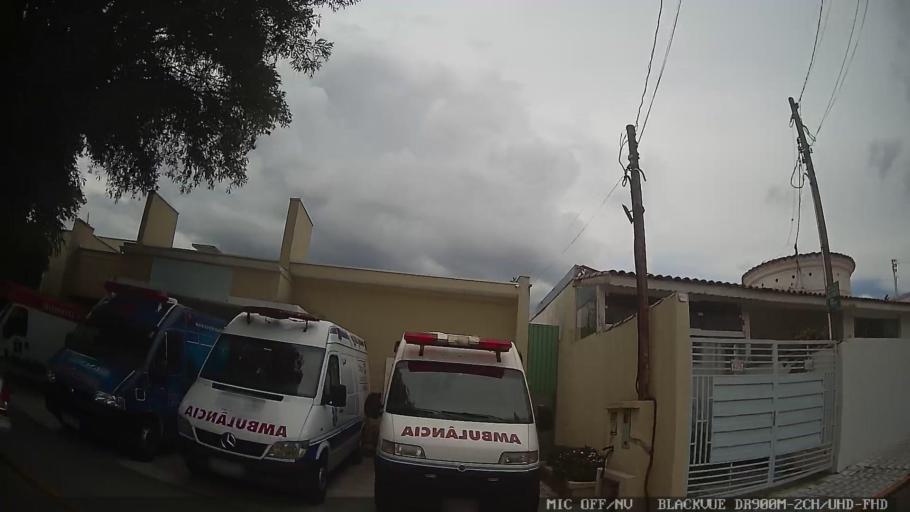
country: BR
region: Sao Paulo
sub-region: Atibaia
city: Atibaia
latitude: -23.1152
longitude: -46.5494
